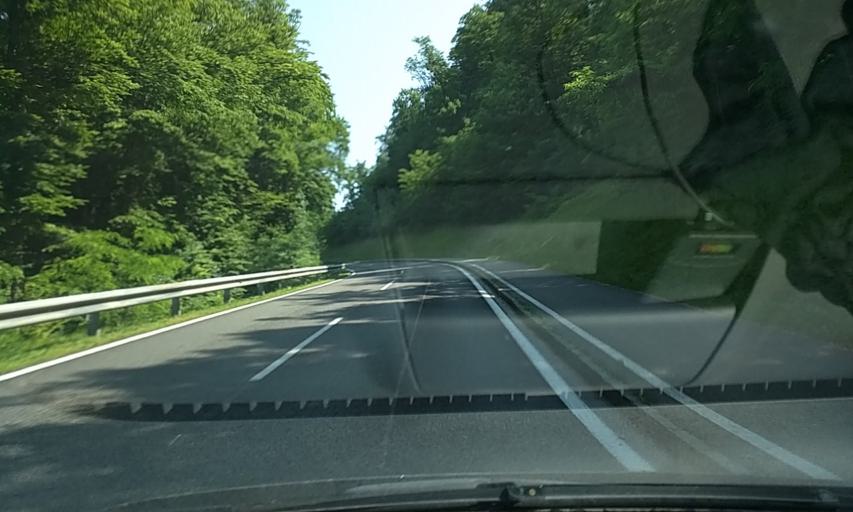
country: AT
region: Lower Austria
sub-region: Politischer Bezirk Krems
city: Aggsbach
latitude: 48.2650
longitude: 15.3797
